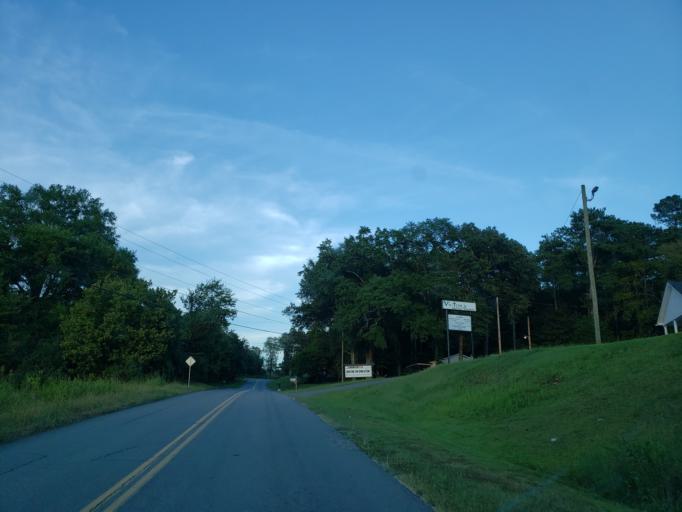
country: US
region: Georgia
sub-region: Floyd County
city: Rome
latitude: 34.2407
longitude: -85.1295
